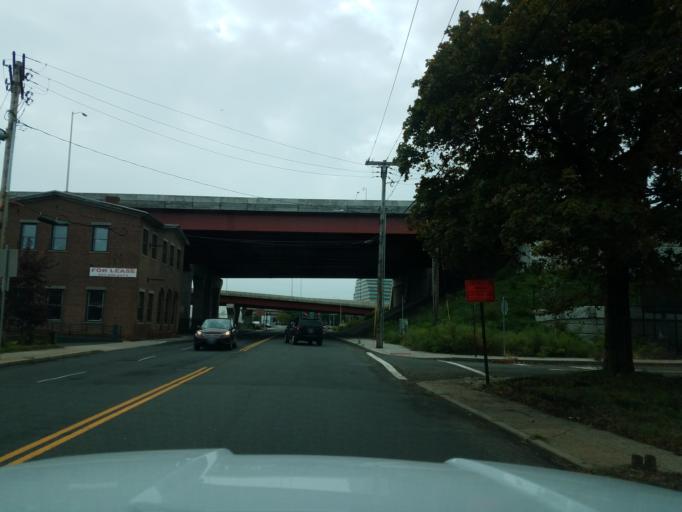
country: US
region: Connecticut
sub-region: New Haven County
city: New Haven
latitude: 41.3028
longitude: -72.9106
